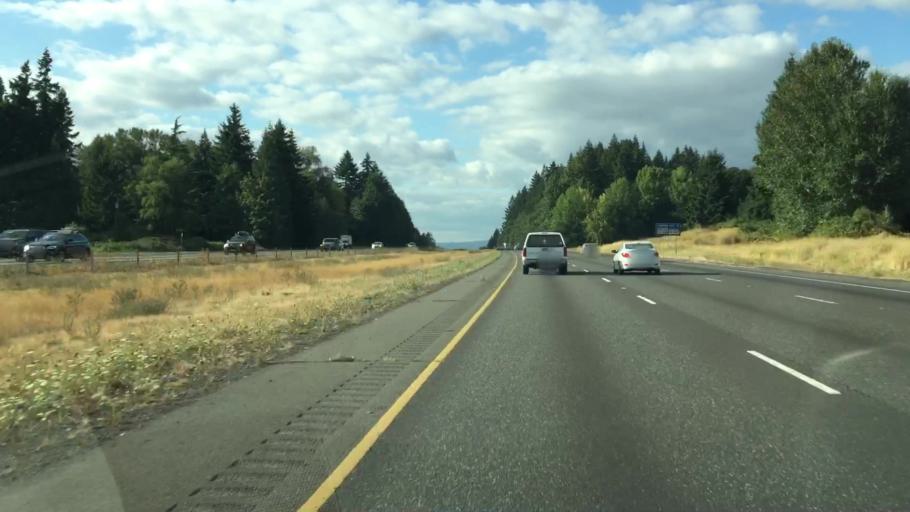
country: US
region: Washington
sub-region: Clark County
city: La Center
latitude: 45.7956
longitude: -122.6765
